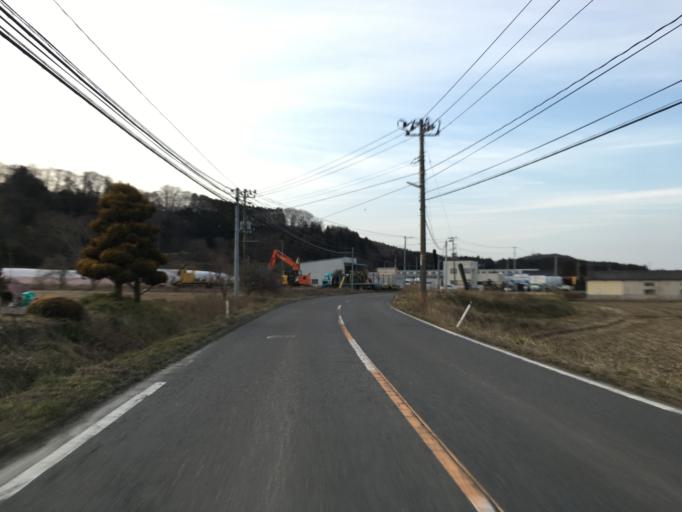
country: JP
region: Ibaraki
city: Daigo
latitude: 36.9376
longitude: 140.4056
